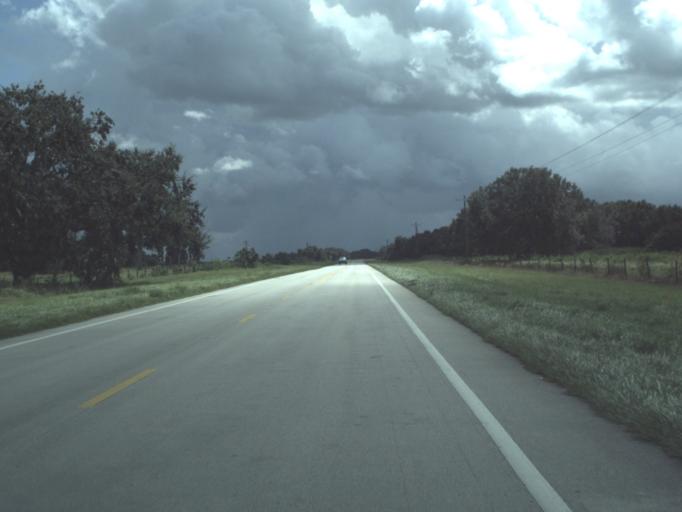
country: US
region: Florida
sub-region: Okeechobee County
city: Okeechobee
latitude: 27.3195
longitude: -80.9148
